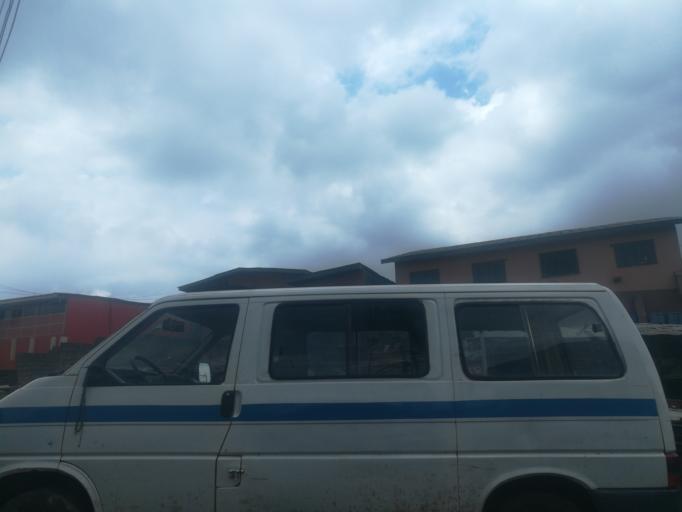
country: NG
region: Lagos
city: Somolu
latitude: 6.5564
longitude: 3.3939
